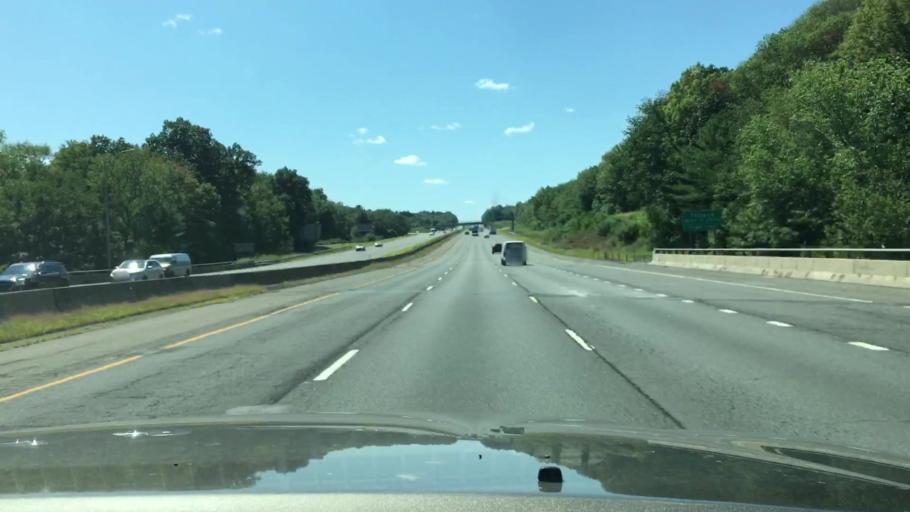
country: US
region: Connecticut
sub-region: Tolland County
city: Stafford Springs
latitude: 41.8908
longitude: -72.3026
